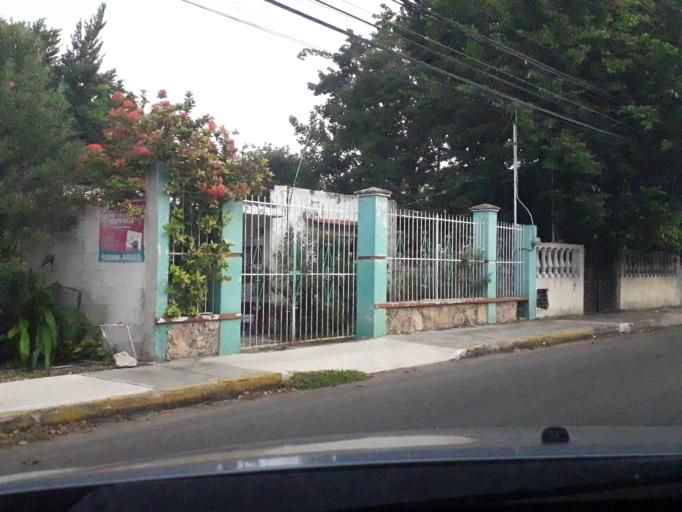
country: MX
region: Yucatan
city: Merida
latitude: 21.0192
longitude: -89.6317
